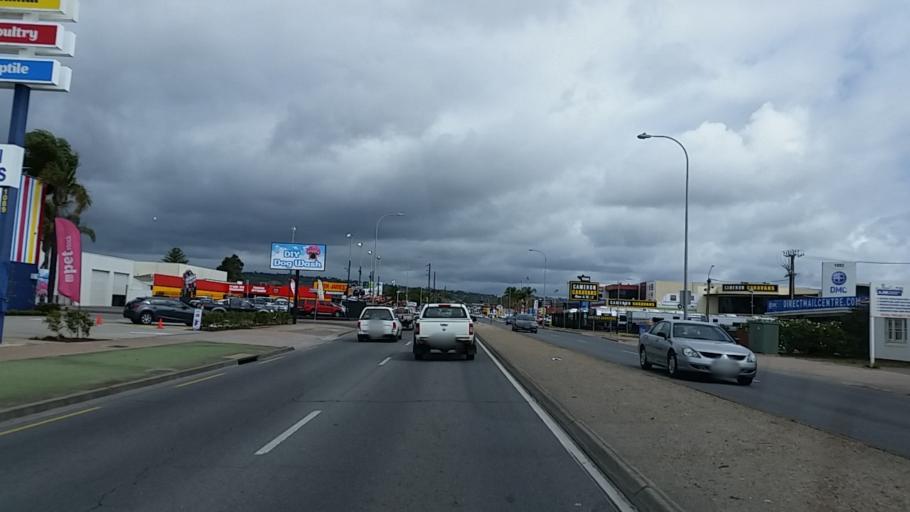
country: AU
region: South Australia
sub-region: Marion
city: Clovelly Park
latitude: -34.9903
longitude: 138.5747
